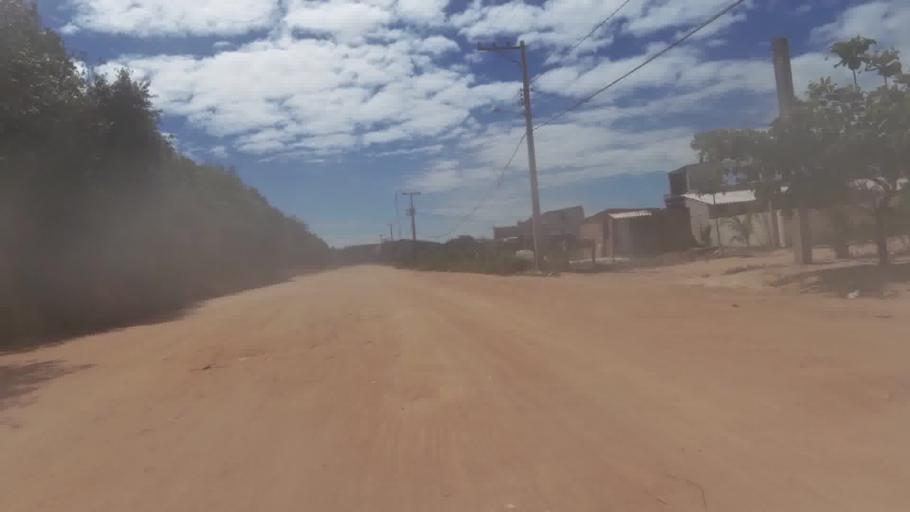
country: BR
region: Espirito Santo
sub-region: Marataizes
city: Marataizes
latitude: -21.1870
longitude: -40.9263
